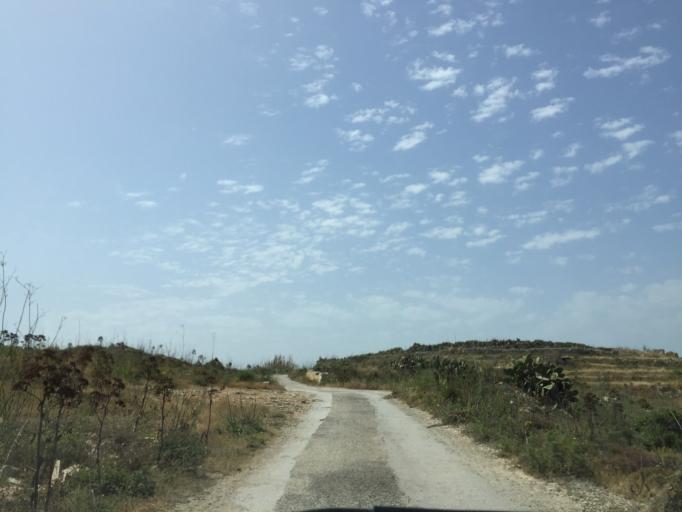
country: MT
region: In-Nadur
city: Nadur
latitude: 36.0613
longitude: 14.2904
